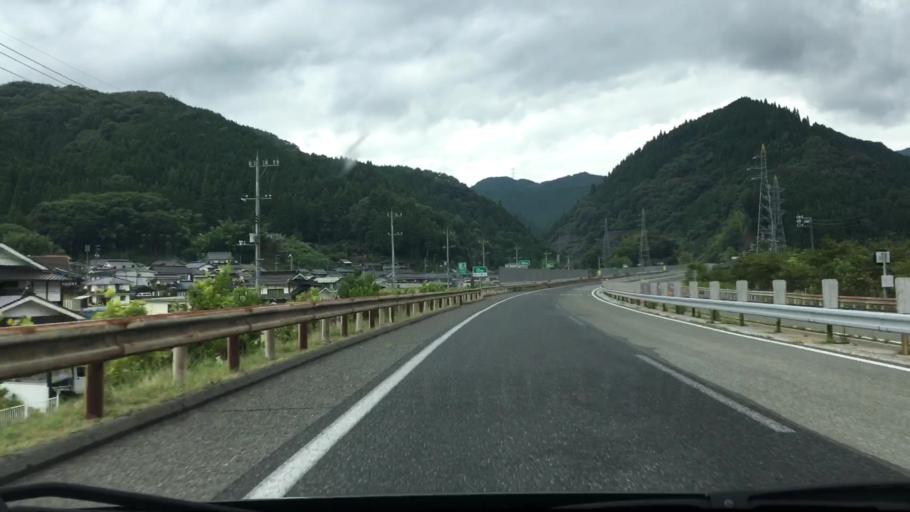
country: JP
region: Okayama
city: Niimi
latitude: 35.0089
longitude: 133.4361
